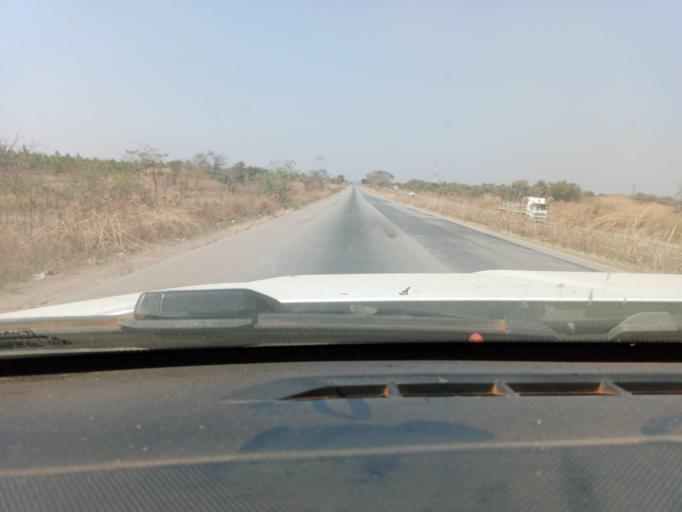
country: ZM
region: Copperbelt
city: Luanshya
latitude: -12.9438
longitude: 28.3763
